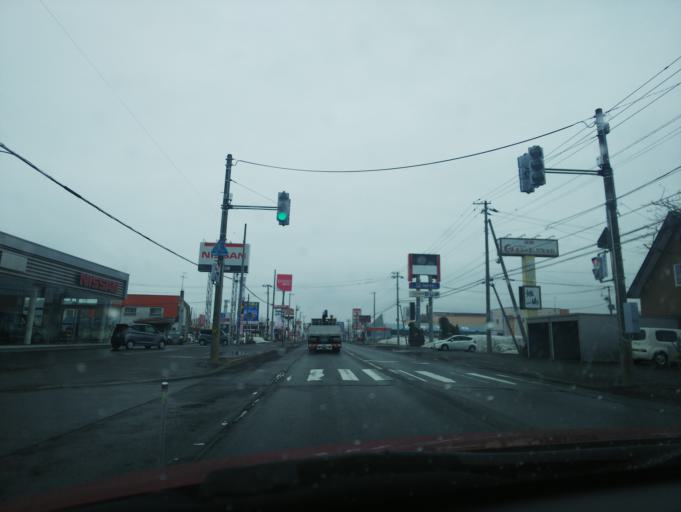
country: JP
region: Hokkaido
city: Nayoro
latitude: 44.1636
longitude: 142.3961
